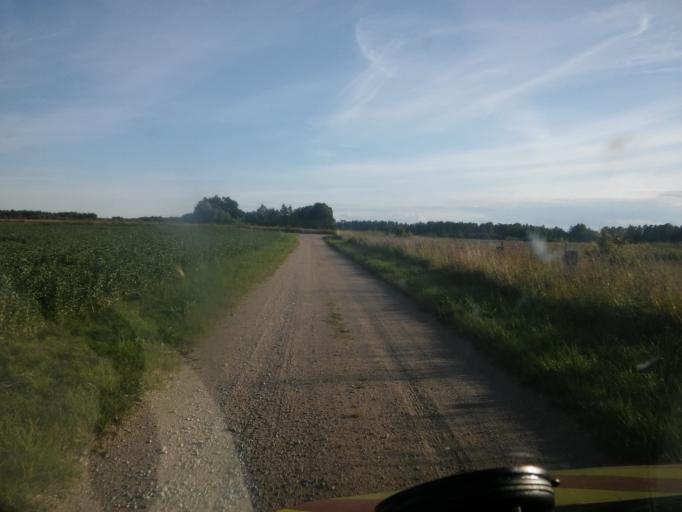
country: EE
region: Valgamaa
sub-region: Torva linn
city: Torva
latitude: 58.0785
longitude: 25.9914
